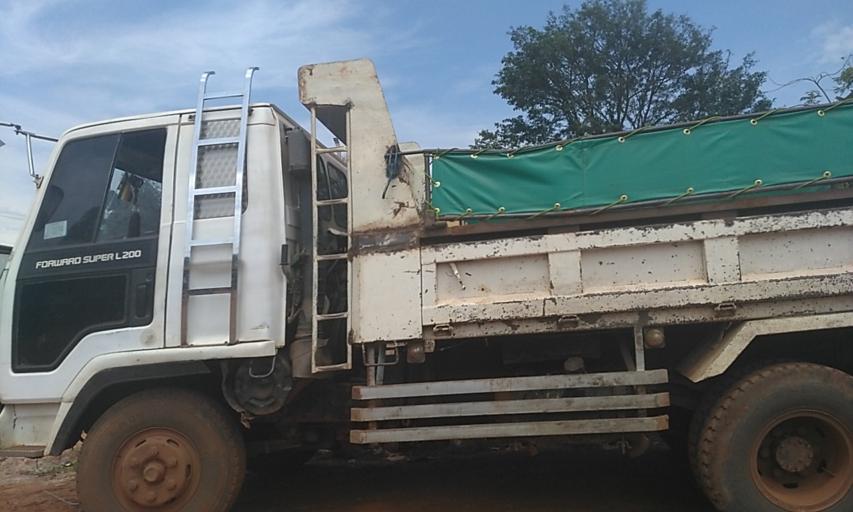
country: UG
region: Central Region
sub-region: Wakiso District
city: Kajansi
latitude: 0.2756
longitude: 32.5148
